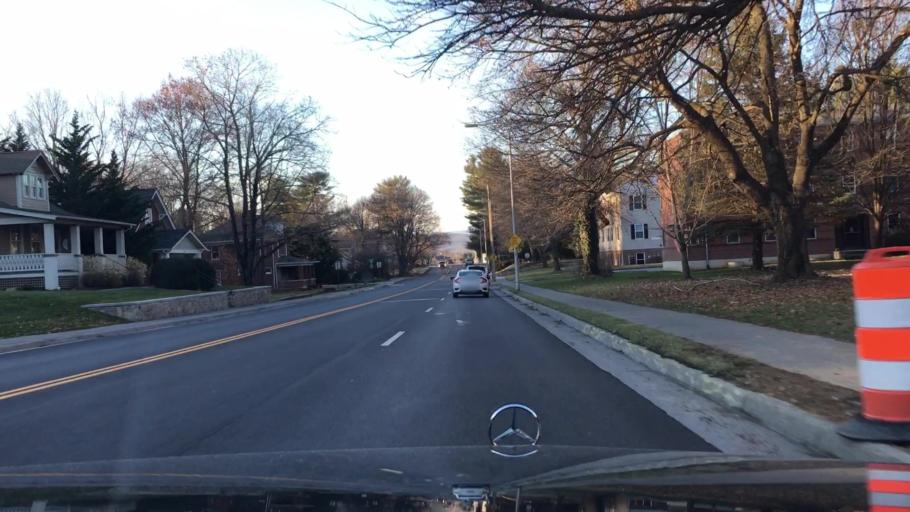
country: US
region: Virginia
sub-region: Montgomery County
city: Blacksburg
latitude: 37.2241
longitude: -80.4082
